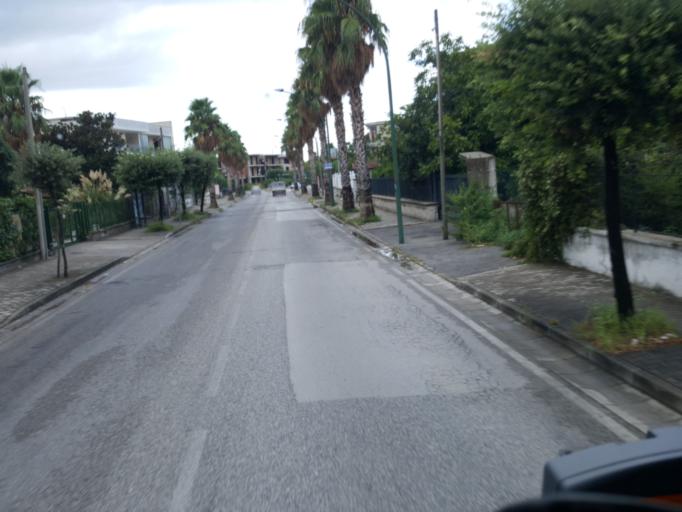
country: IT
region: Campania
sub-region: Provincia di Napoli
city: Palma Campania
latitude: 40.8591
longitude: 14.5504
